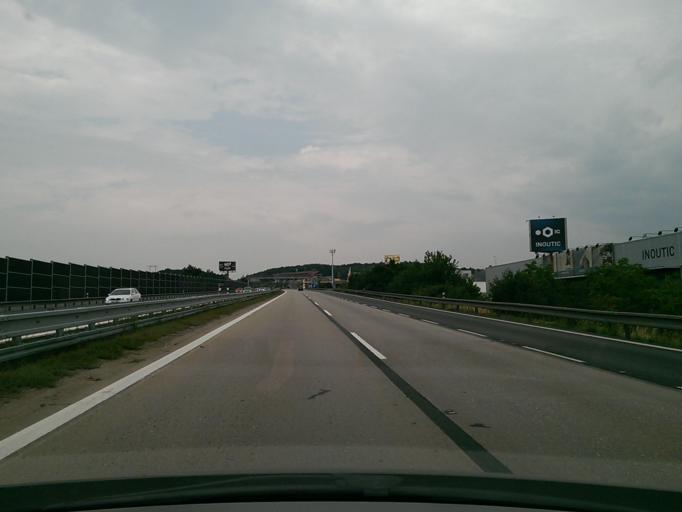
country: CZ
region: South Moravian
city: Troubsko
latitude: 49.1802
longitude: 16.4861
